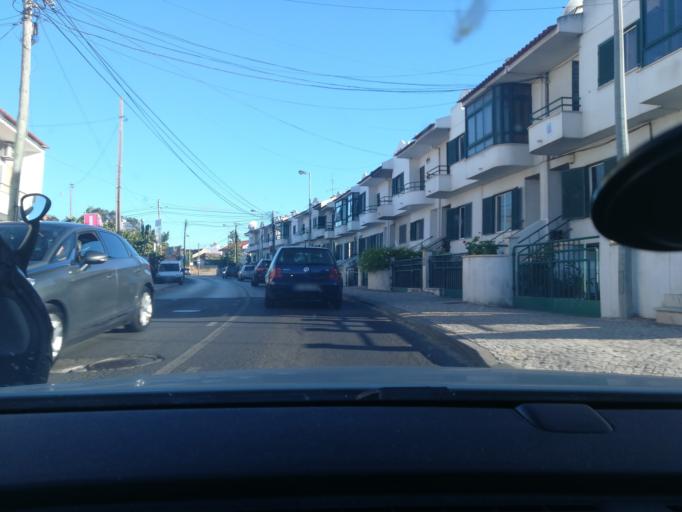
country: PT
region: Setubal
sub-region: Seixal
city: Corroios
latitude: 38.6466
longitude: -9.1600
